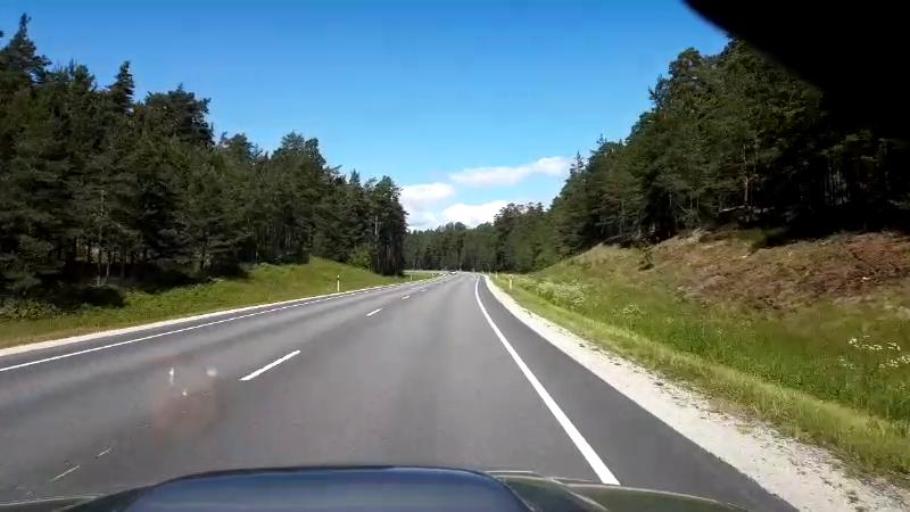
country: EE
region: Paernumaa
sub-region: Paernu linn
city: Parnu
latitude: 58.1434
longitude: 24.5057
